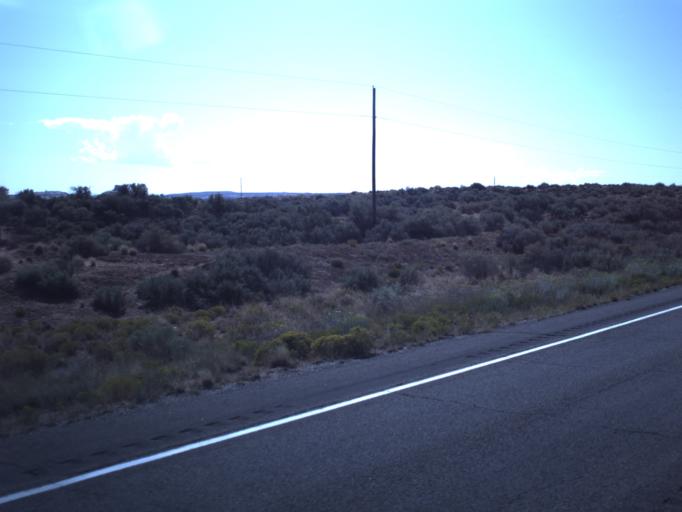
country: US
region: Utah
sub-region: San Juan County
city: Blanding
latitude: 37.0929
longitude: -109.5479
